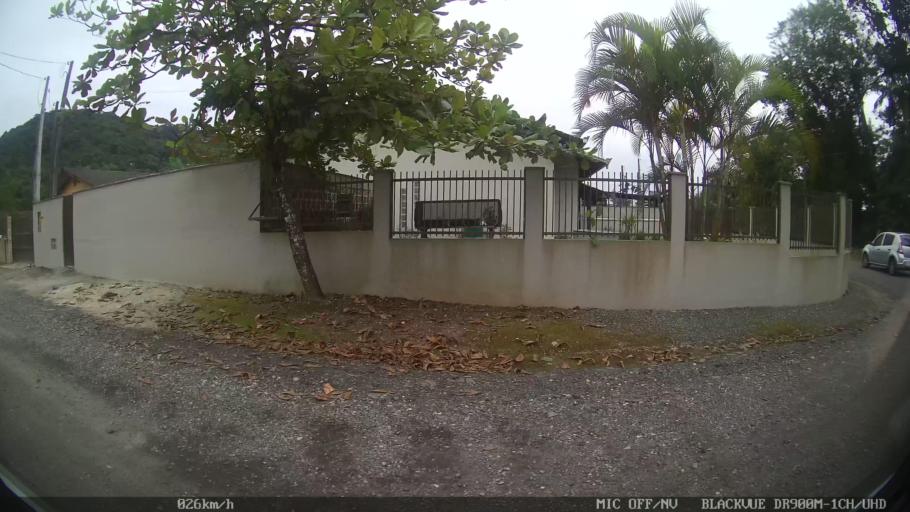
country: BR
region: Santa Catarina
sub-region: Joinville
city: Joinville
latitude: -26.2128
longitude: -48.9133
